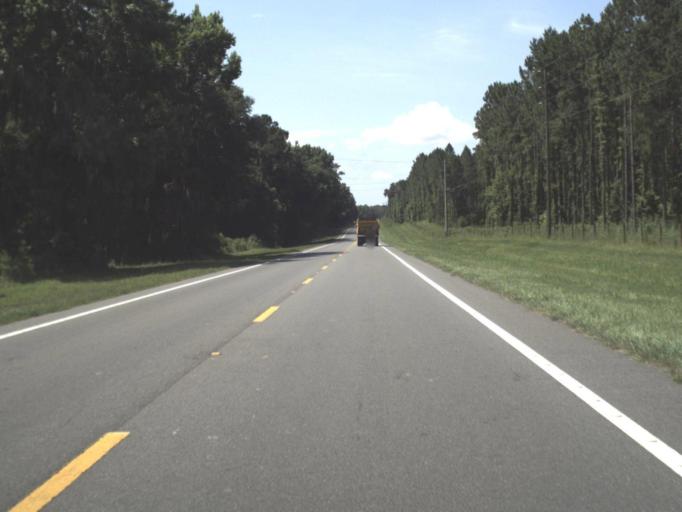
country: US
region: Florida
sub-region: Alachua County
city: Archer
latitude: 29.5072
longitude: -82.4065
